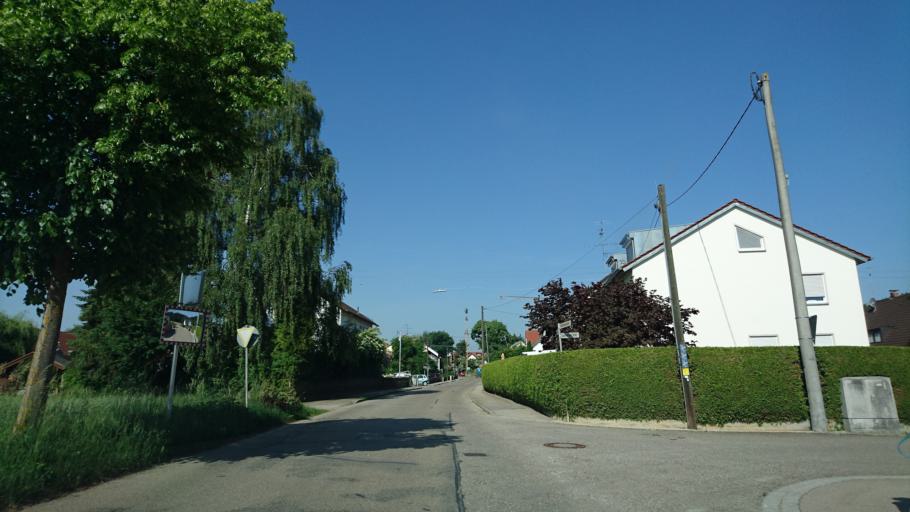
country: DE
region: Bavaria
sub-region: Swabia
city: Diedorf
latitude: 48.3568
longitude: 10.7502
